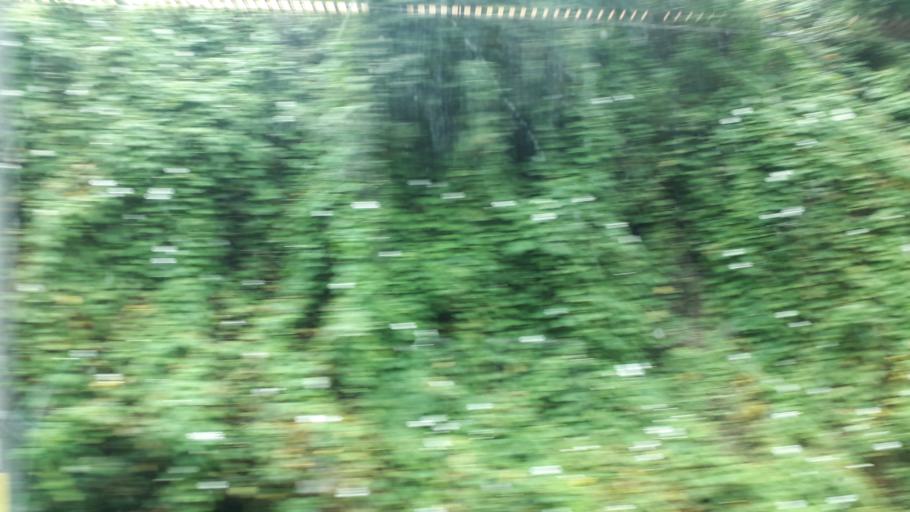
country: IE
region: Leinster
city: Malahide
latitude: 53.4434
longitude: -6.1568
